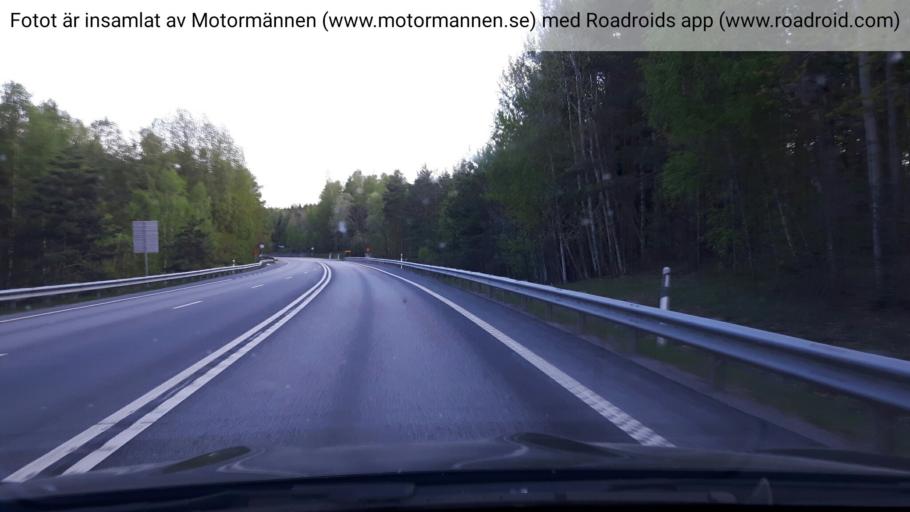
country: SE
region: Stockholm
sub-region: Lidingo
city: Brevik
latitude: 59.4359
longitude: 18.2198
